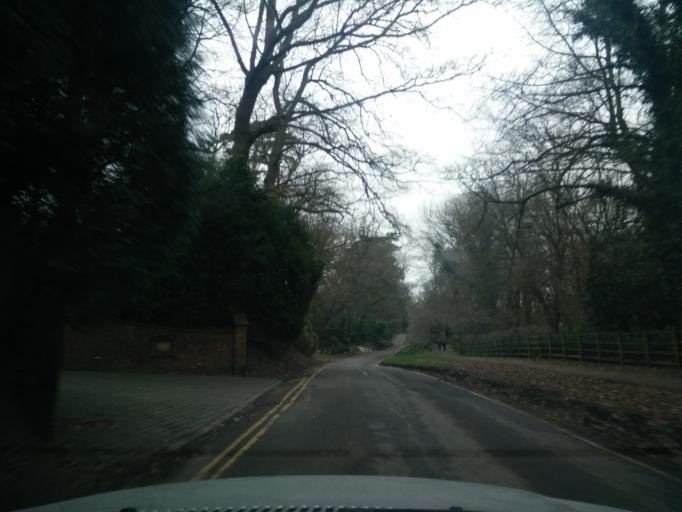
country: GB
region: England
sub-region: Buckinghamshire
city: Little Chalfont
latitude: 51.6610
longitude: -0.5593
